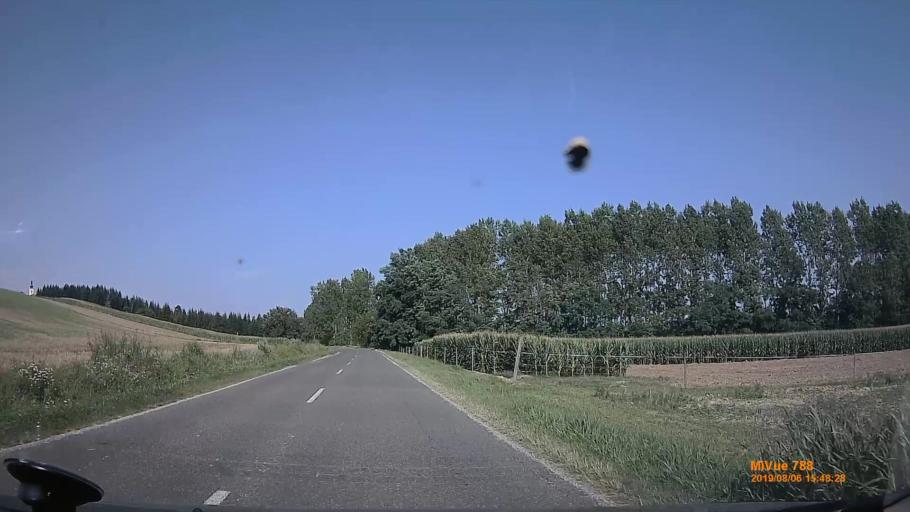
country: HU
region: Somogy
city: Csurgo
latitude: 46.2677
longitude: 17.0354
